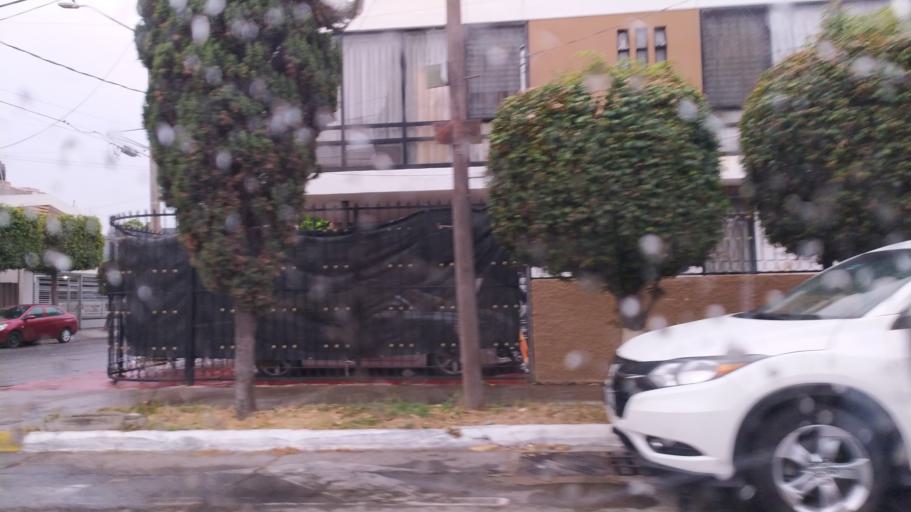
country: MX
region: Jalisco
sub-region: Zapopan
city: Zapopan
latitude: 20.7111
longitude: -103.3662
